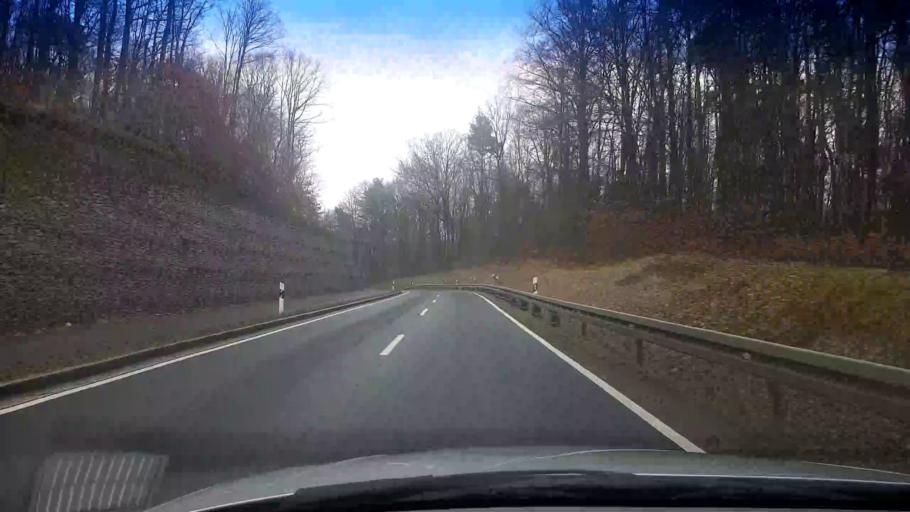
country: DE
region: Bavaria
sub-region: Regierungsbezirk Unterfranken
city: Sand
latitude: 49.9567
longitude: 10.5784
